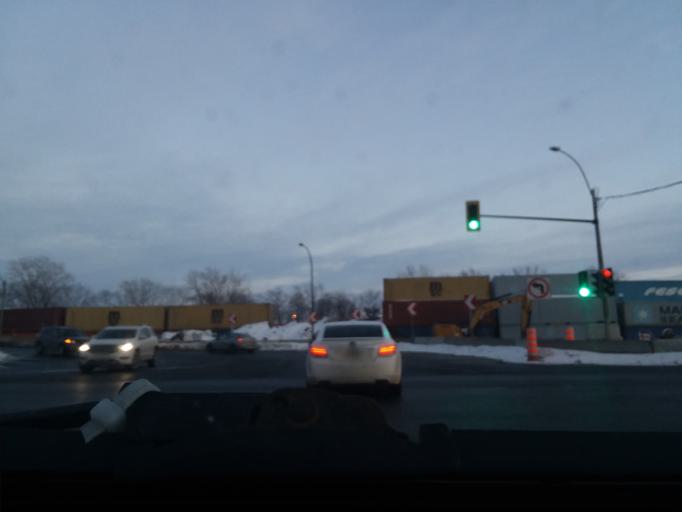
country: CA
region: Quebec
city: Montreal-Ouest
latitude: 45.4516
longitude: -73.6286
